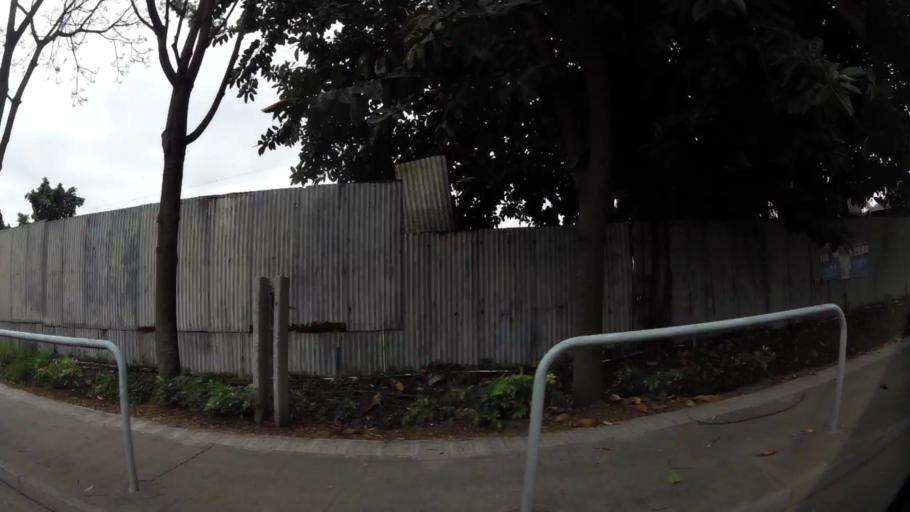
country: HK
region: Tuen Mun
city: Tuen Mun
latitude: 22.4235
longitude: 113.9929
